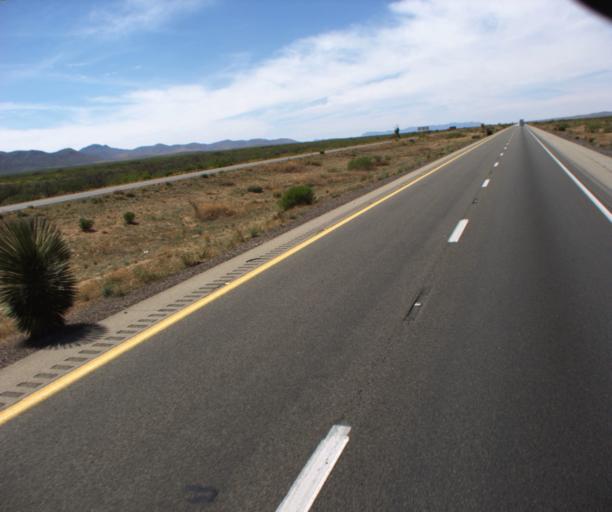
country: US
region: Arizona
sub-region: Cochise County
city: Willcox
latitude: 32.3364
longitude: -109.5398
